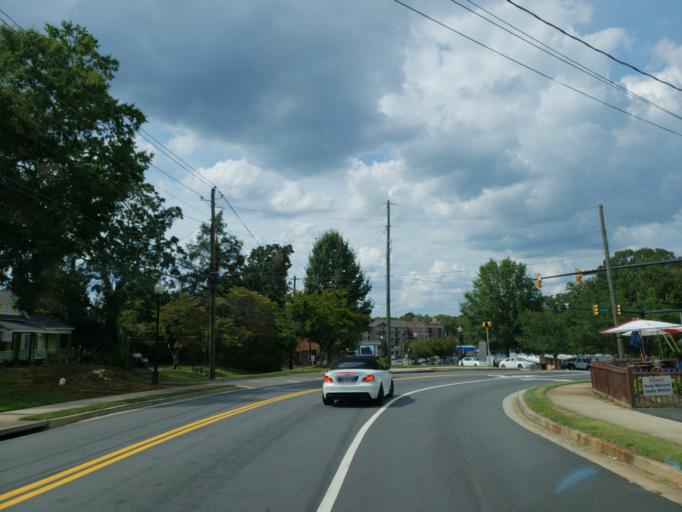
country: US
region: Georgia
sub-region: Cobb County
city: Kennesaw
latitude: 34.0200
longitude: -84.6141
